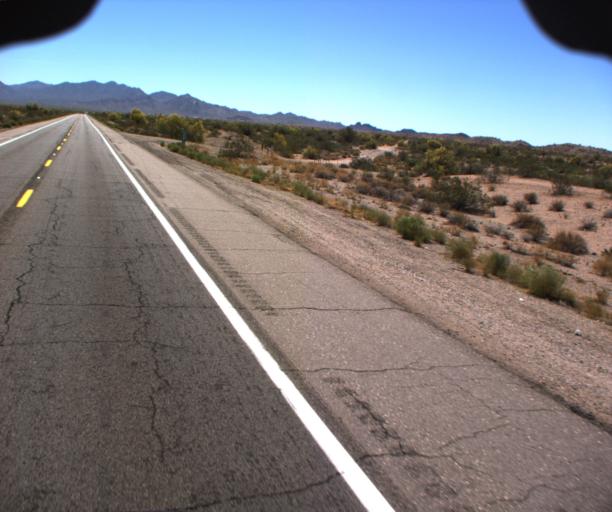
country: US
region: Arizona
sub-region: Mohave County
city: Desert Hills
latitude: 34.7168
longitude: -114.3099
